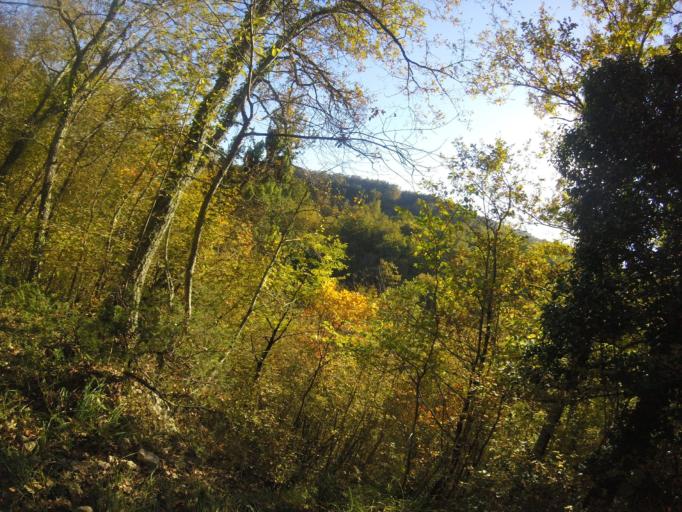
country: HR
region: Istarska
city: Pazin
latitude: 45.2202
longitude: 14.0285
